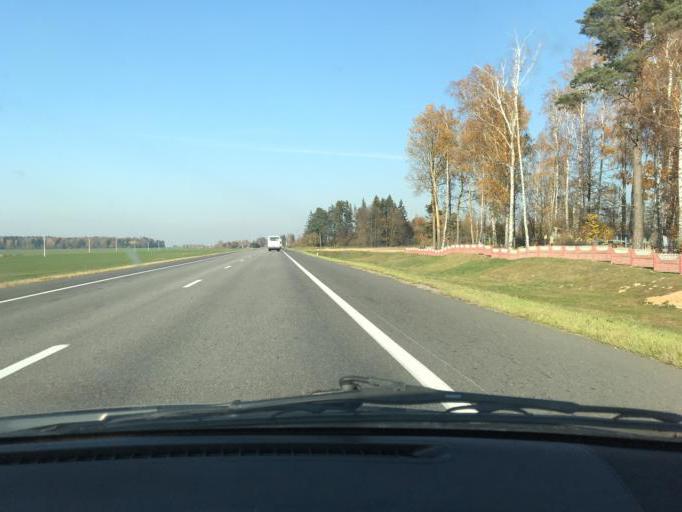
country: BY
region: Vitebsk
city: Balbasava
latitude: 54.3213
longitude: 30.4471
